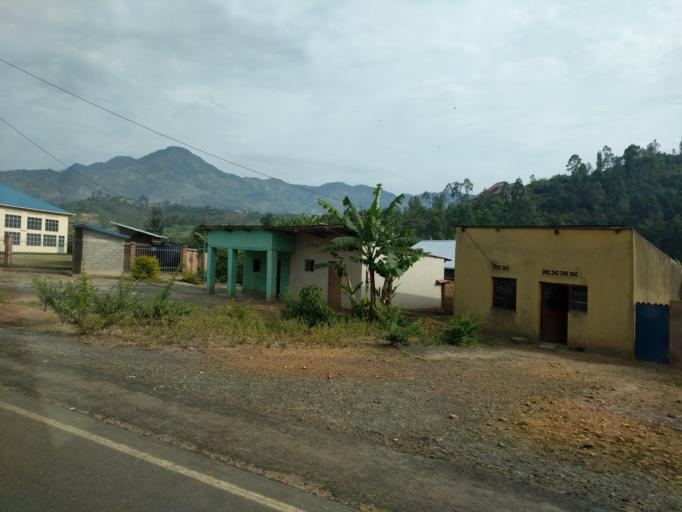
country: RW
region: Northern Province
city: Musanze
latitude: -1.6566
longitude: 29.8247
